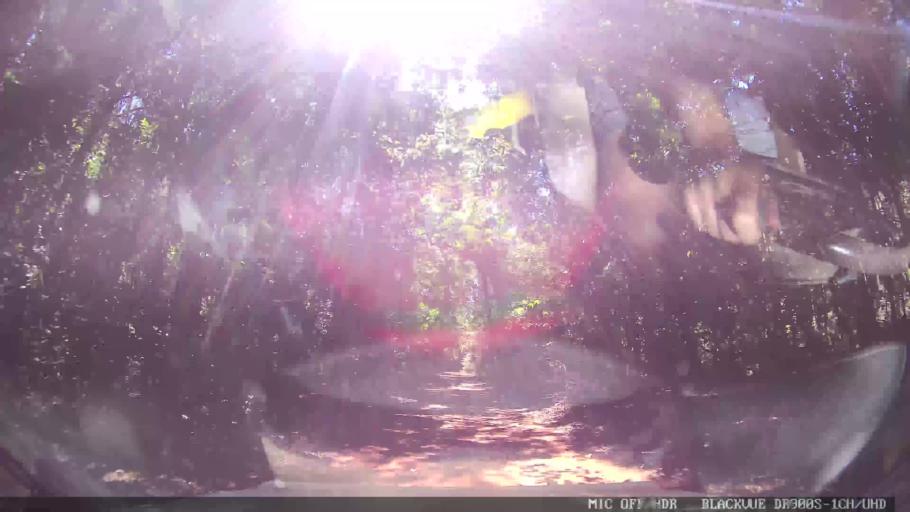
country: AU
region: Queensland
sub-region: Torres
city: Thursday Island
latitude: -10.7787
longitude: 142.4898
